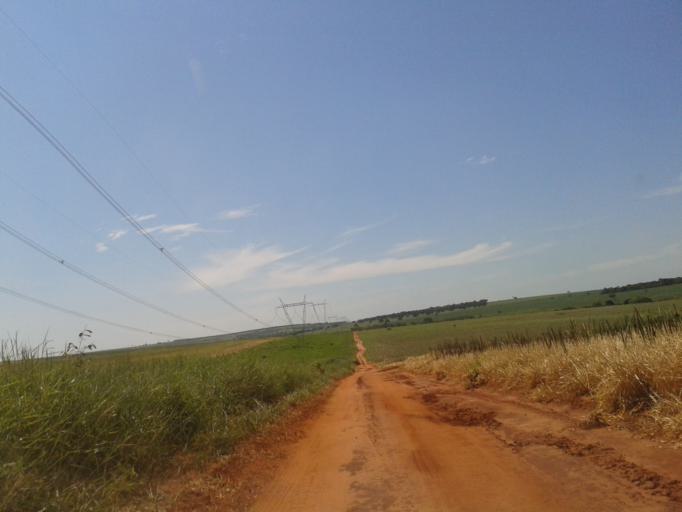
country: BR
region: Minas Gerais
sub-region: Santa Vitoria
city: Santa Vitoria
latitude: -19.0878
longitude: -50.4526
